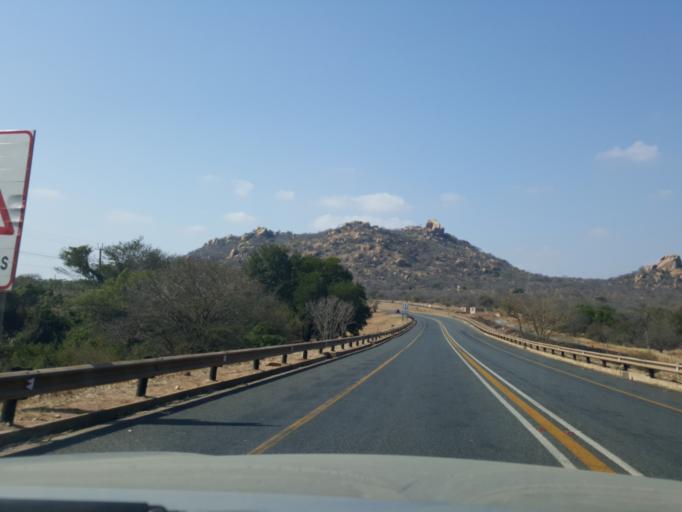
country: ZA
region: Mpumalanga
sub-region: Ehlanzeni District
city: Komatipoort
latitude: -25.4610
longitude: 31.6139
